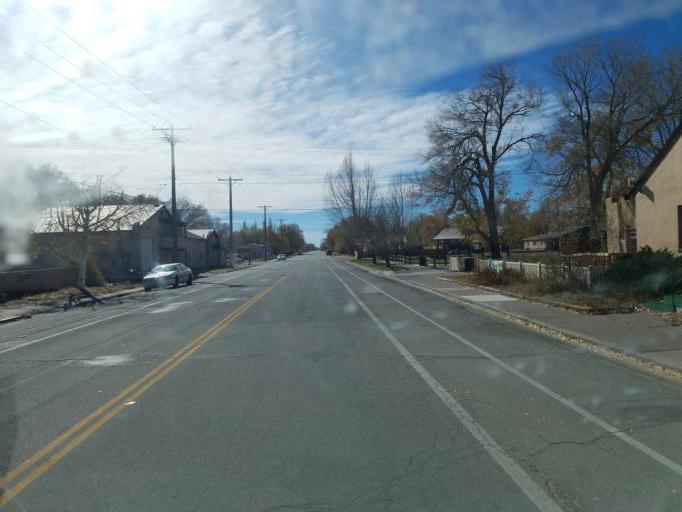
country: US
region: Colorado
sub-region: Alamosa County
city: Alamosa
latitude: 37.4643
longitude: -105.8702
